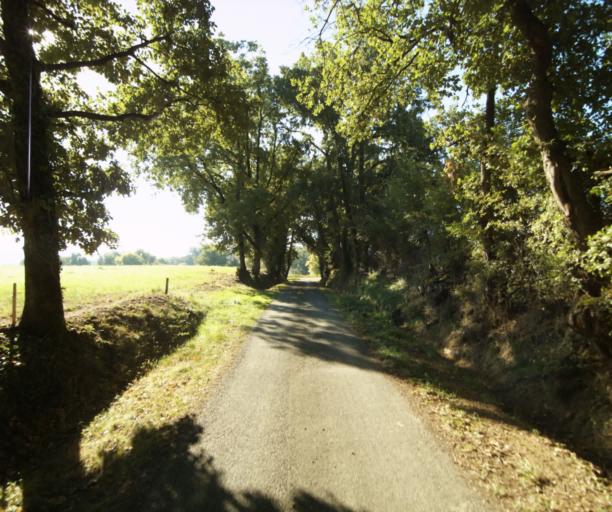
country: FR
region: Midi-Pyrenees
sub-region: Departement du Gers
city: Vic-Fezensac
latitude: 43.8218
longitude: 0.2826
